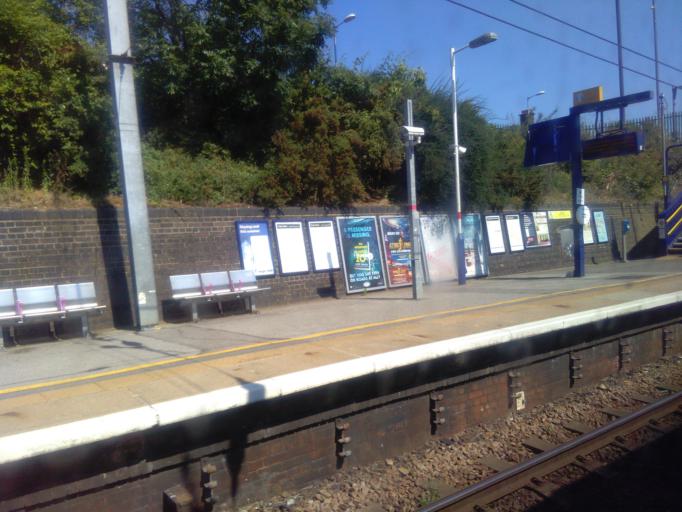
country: GB
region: England
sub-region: Central Bedfordshire
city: Flitwick
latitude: 52.0036
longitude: -0.4945
